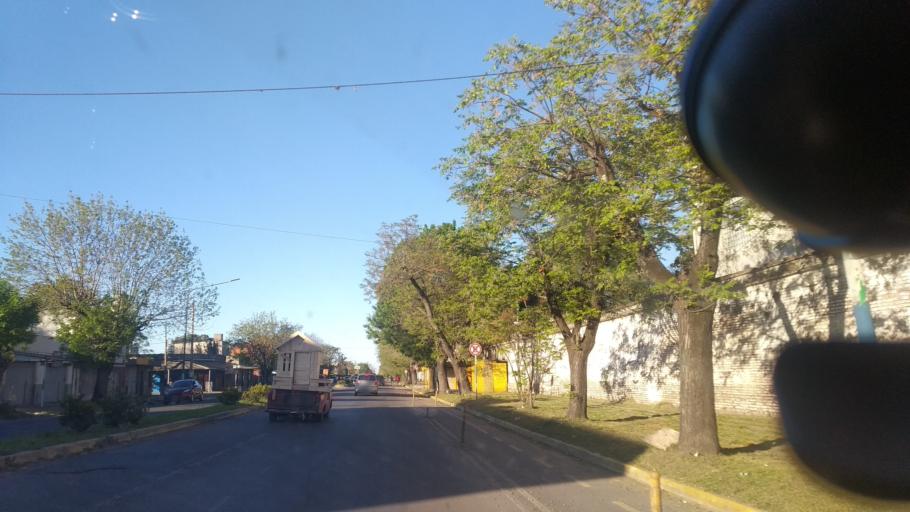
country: AR
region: Buenos Aires
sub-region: Partido de La Plata
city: La Plata
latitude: -34.9564
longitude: -57.9557
